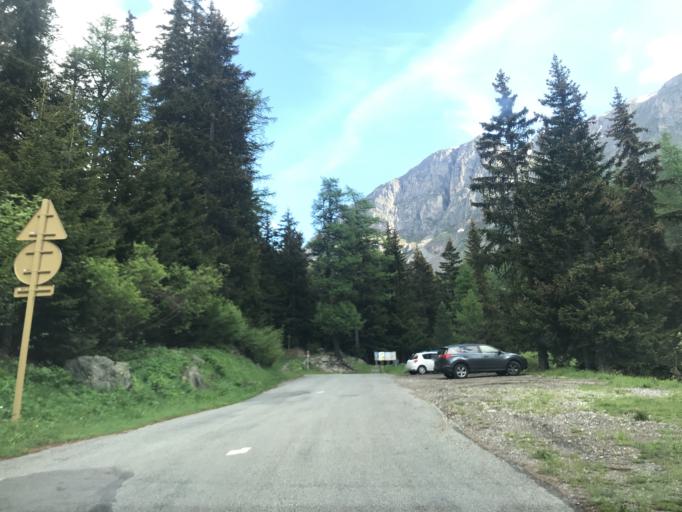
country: FR
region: Rhone-Alpes
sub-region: Departement de la Savoie
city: Modane
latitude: 45.2242
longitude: 6.6515
